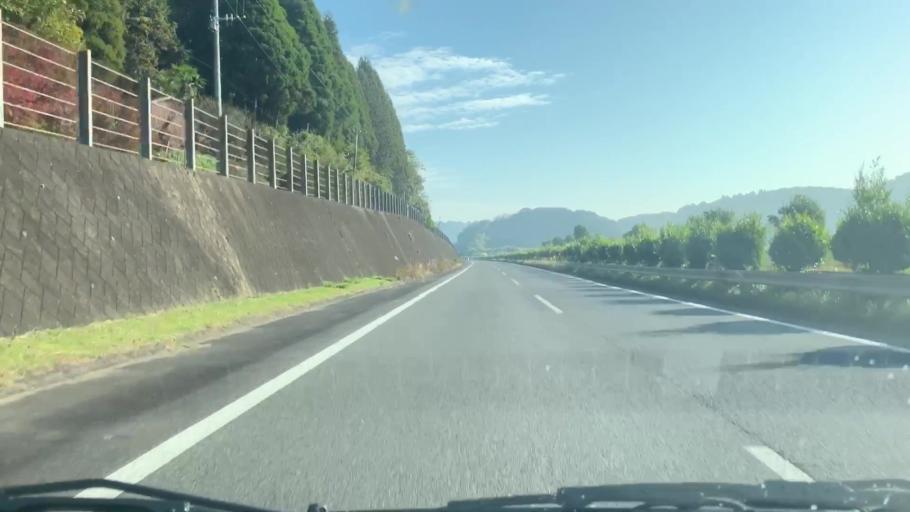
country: JP
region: Saga Prefecture
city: Takeocho-takeo
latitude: 33.2713
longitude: 130.1010
